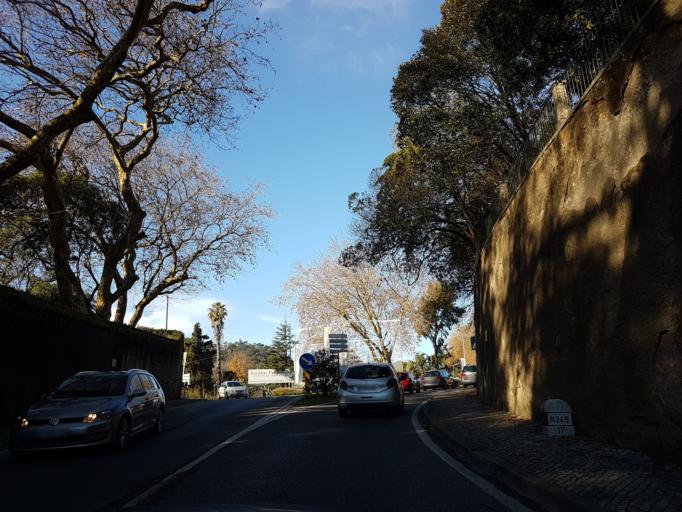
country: PT
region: Lisbon
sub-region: Sintra
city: Sintra
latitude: 38.7868
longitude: -9.3726
